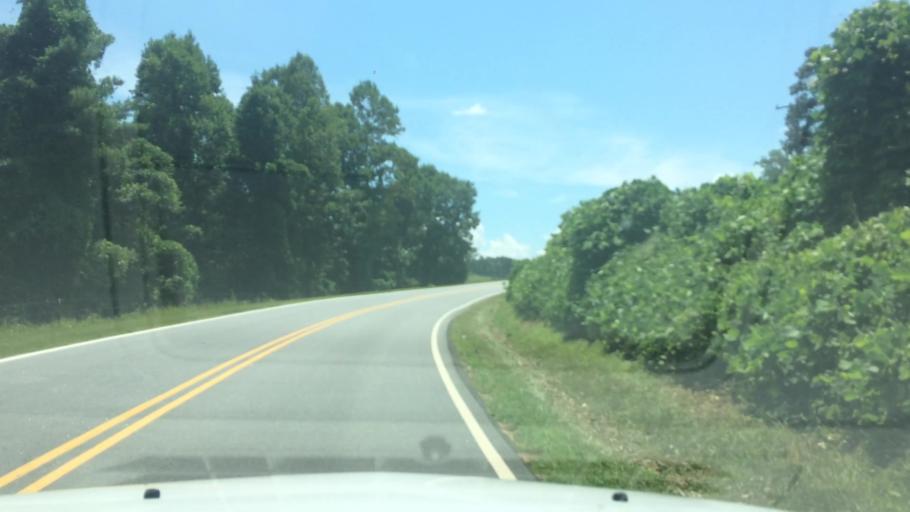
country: US
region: North Carolina
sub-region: Alexander County
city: Taylorsville
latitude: 35.9317
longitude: -81.2638
